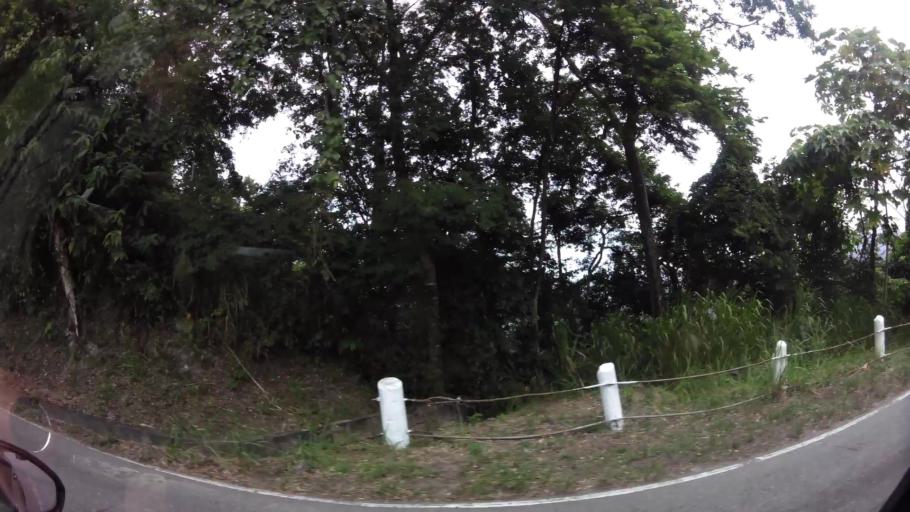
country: TT
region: Diego Martin
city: Petit Valley
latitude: 10.7306
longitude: -61.4921
